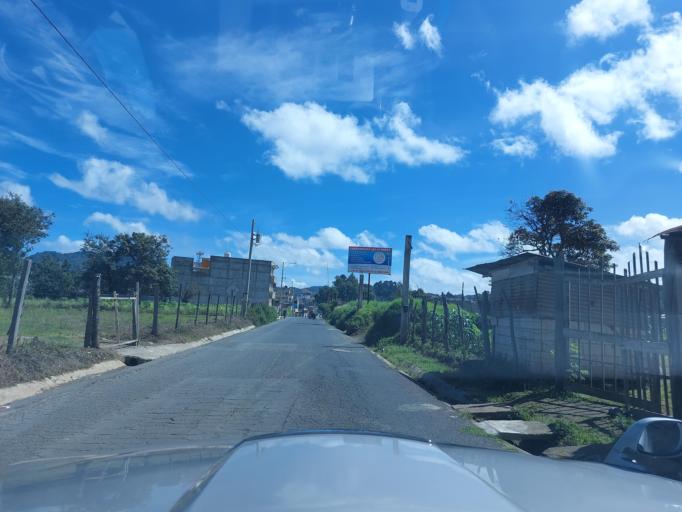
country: GT
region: Chimaltenango
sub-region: Municipio de San Juan Comalapa
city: Comalapa
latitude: 14.7266
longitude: -90.8876
